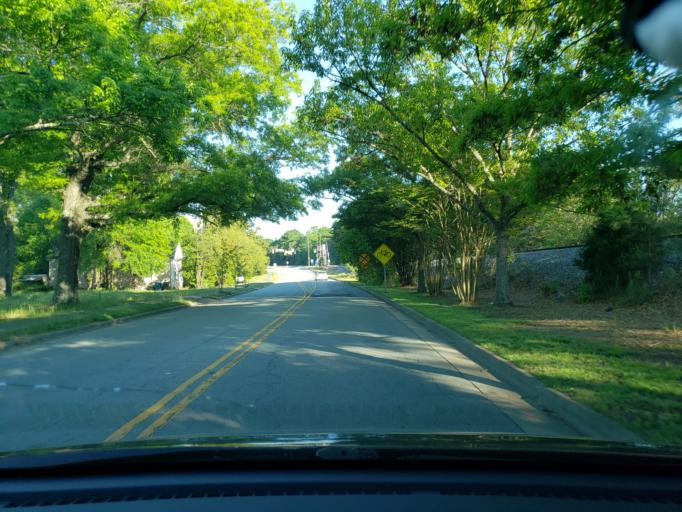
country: US
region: North Carolina
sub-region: Durham County
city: Durham
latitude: 36.0092
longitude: -78.9308
